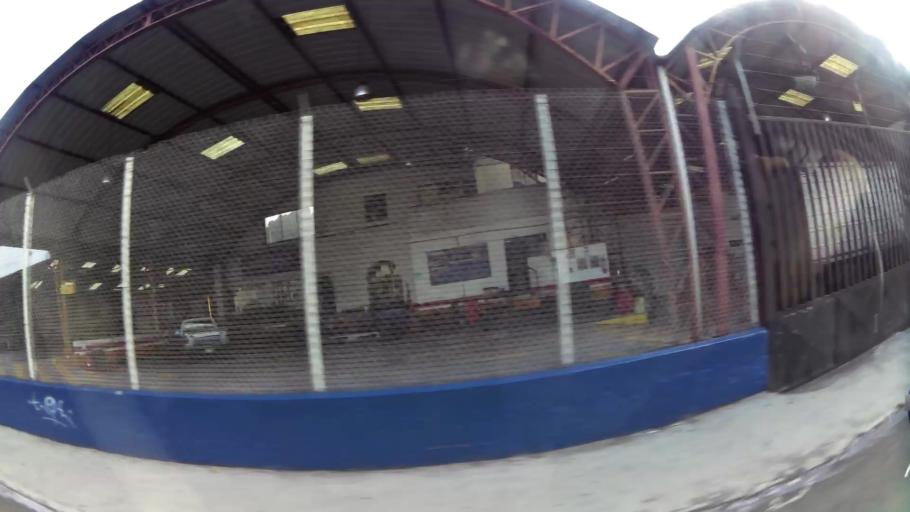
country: EC
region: Pichincha
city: Quito
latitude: -0.2112
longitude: -78.4932
